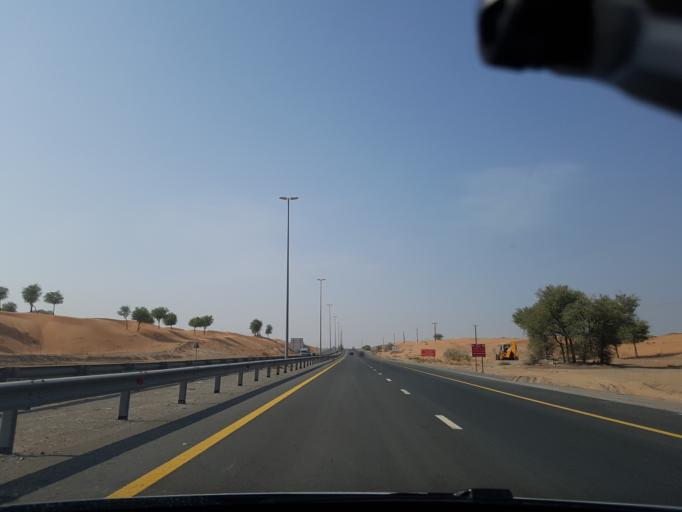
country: AE
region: Umm al Qaywayn
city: Umm al Qaywayn
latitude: 25.5156
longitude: 55.7448
